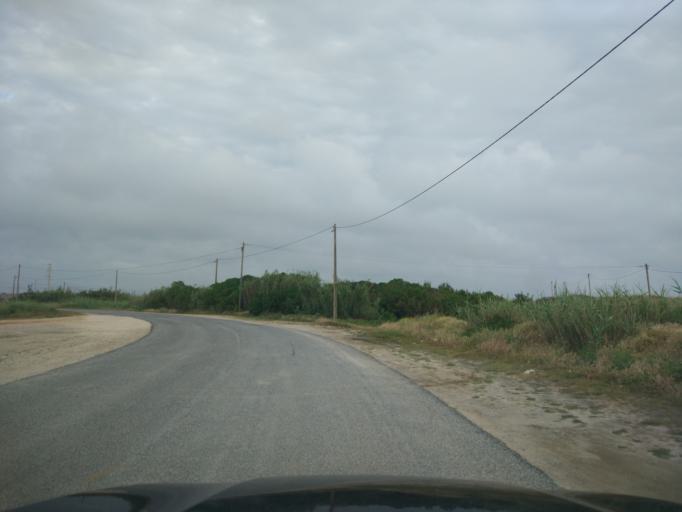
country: PT
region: Leiria
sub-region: Peniche
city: Peniche
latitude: 39.3498
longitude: -9.3650
